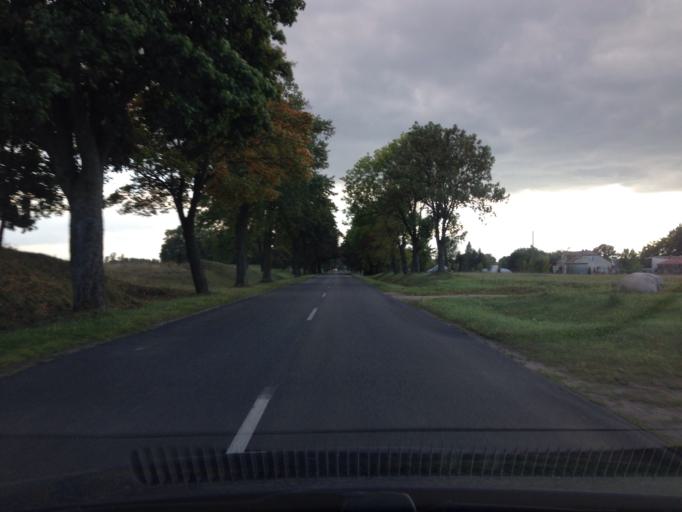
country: PL
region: Kujawsko-Pomorskie
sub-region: Powiat rypinski
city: Rogowo
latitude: 52.9775
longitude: 19.3299
